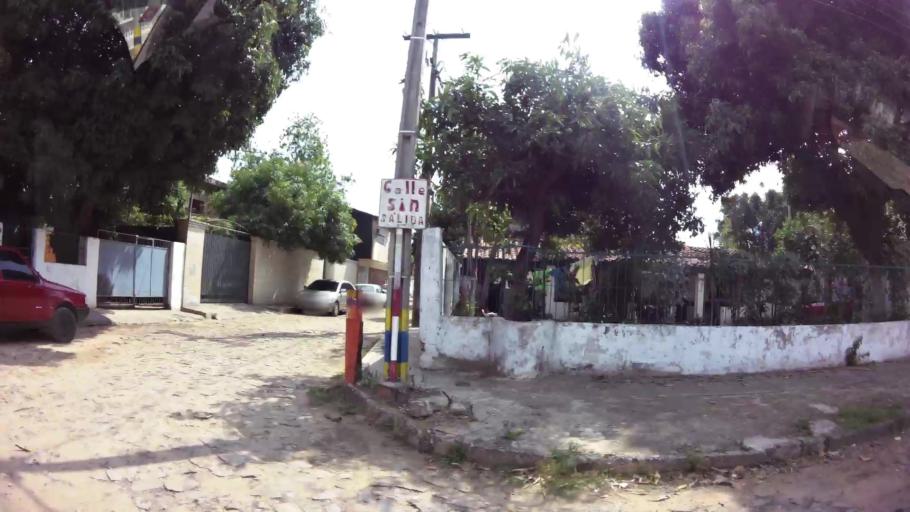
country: PY
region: Asuncion
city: Asuncion
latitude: -25.2599
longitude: -57.5851
